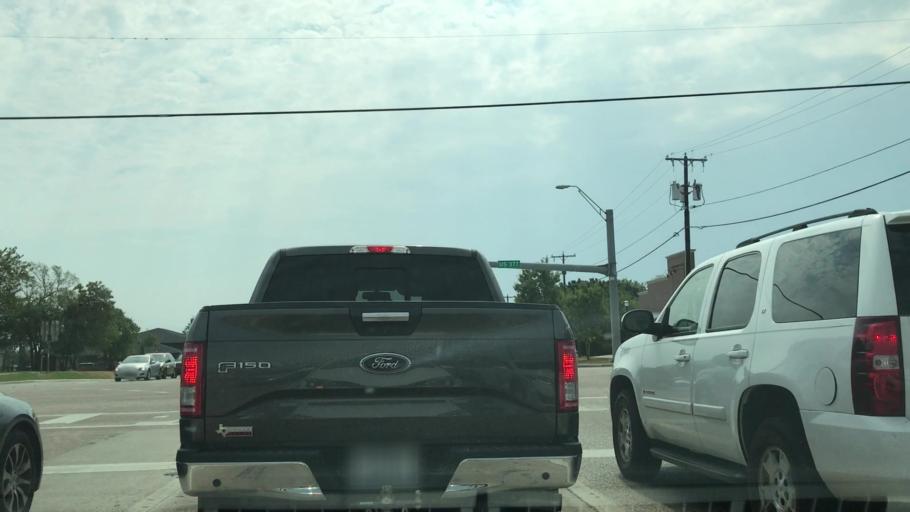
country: US
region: Texas
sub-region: Tarrant County
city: Keller
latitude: 32.9346
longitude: -97.2539
